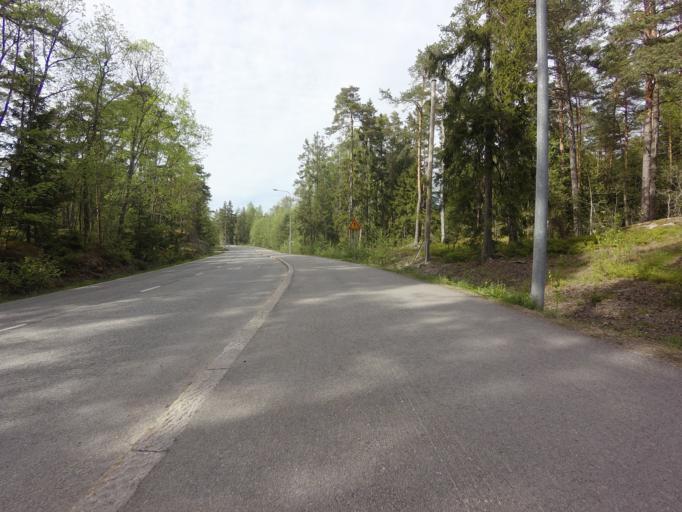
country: FI
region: Uusimaa
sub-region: Helsinki
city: Koukkuniemi
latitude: 60.1237
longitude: 24.7143
